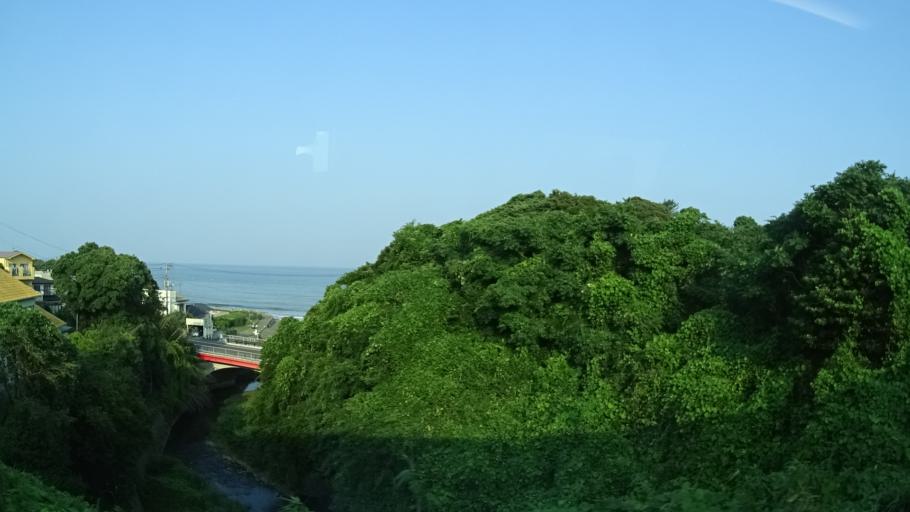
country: JP
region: Ibaraki
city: Hitachi
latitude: 36.5711
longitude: 140.6500
